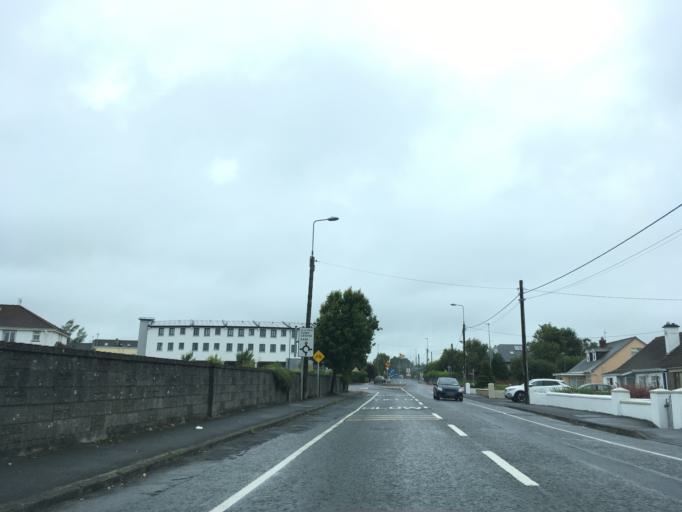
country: IE
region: Munster
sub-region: An Clar
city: Ennis
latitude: 52.8279
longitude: -8.9789
